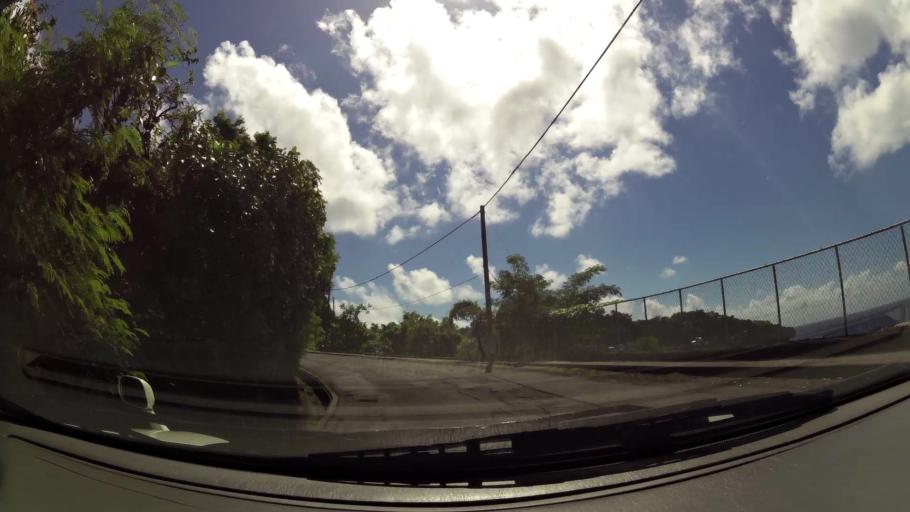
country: VC
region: Saint George
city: Kingstown
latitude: 13.1563
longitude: -61.2205
